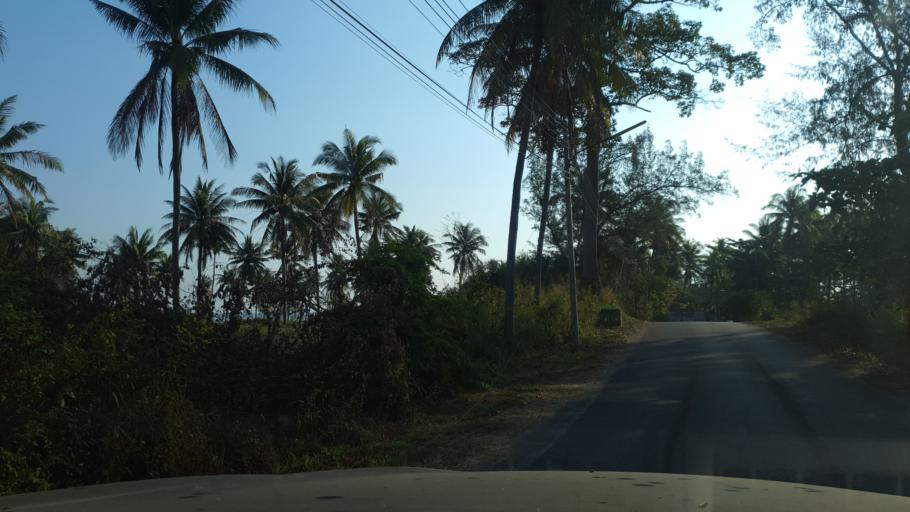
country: TH
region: Prachuap Khiri Khan
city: Bang Saphan
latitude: 11.2126
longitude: 99.5770
